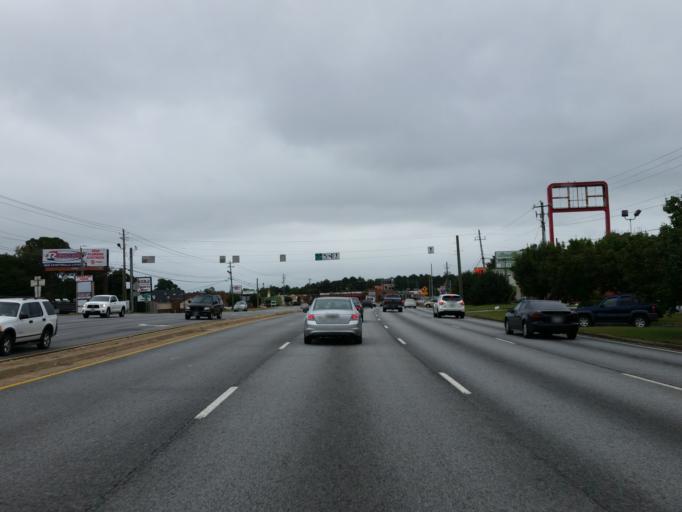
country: US
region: Georgia
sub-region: Clayton County
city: Morrow
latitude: 33.5780
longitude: -84.3735
